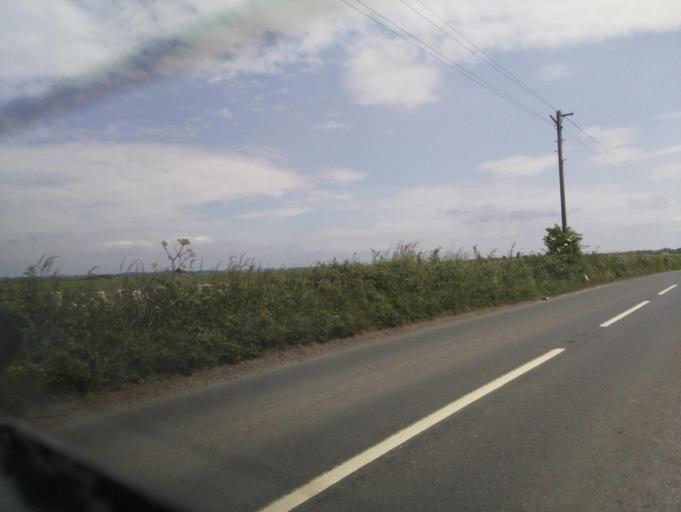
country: GB
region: Wales
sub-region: Vale of Glamorgan
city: Wick
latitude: 51.4530
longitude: -3.5842
